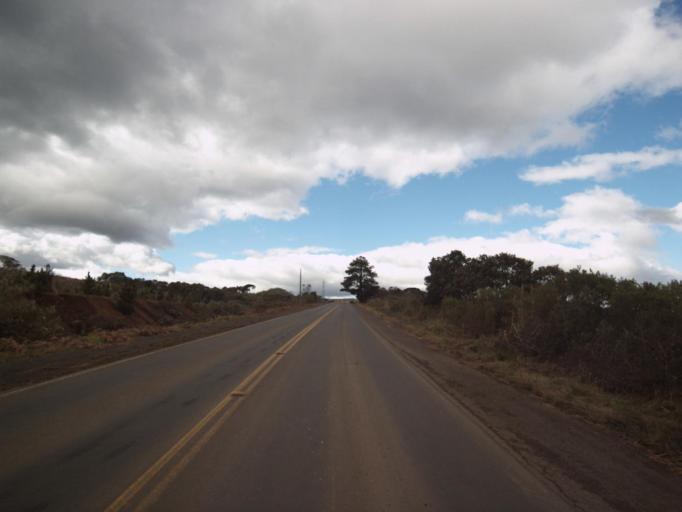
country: BR
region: Santa Catarina
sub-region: Joacaba
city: Joacaba
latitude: -27.0984
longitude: -51.6556
